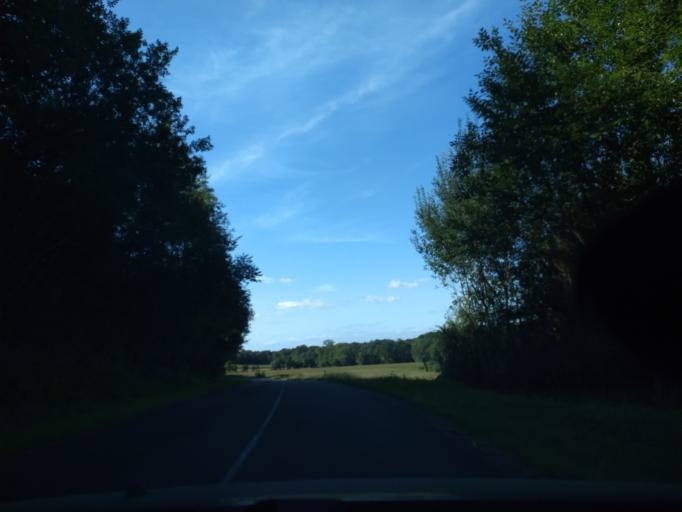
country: FR
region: Aquitaine
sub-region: Departement des Pyrenees-Atlantiques
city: Soumoulou
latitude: 43.2923
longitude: -0.1503
